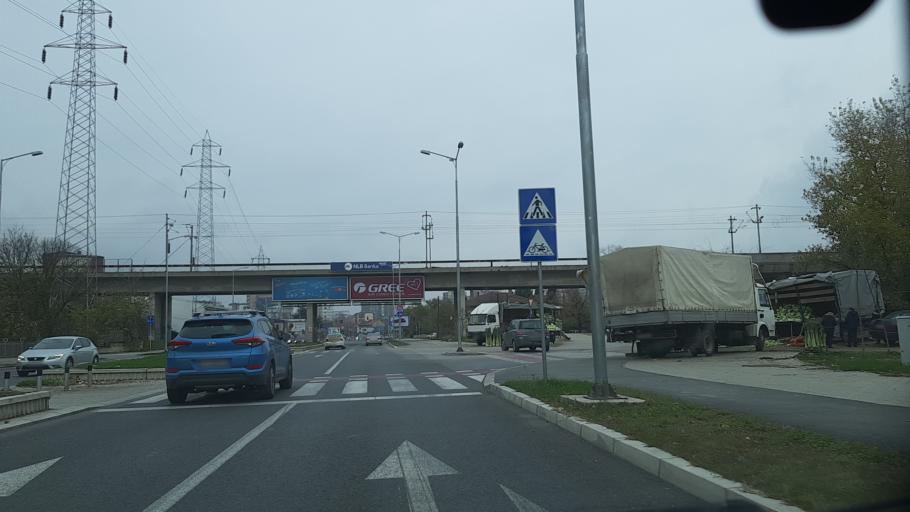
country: MK
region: Karpos
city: Skopje
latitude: 41.9873
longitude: 21.4432
